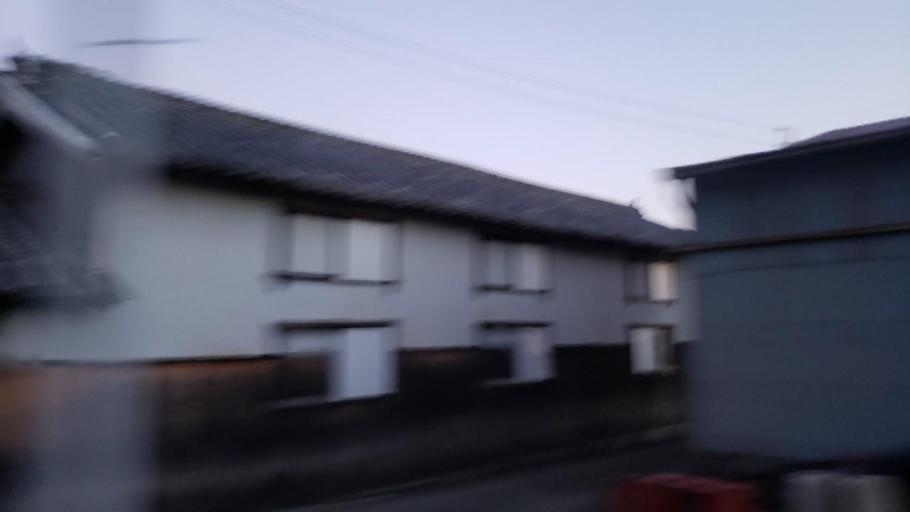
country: JP
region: Tokushima
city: Kamojimacho-jogejima
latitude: 34.1070
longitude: 134.3244
